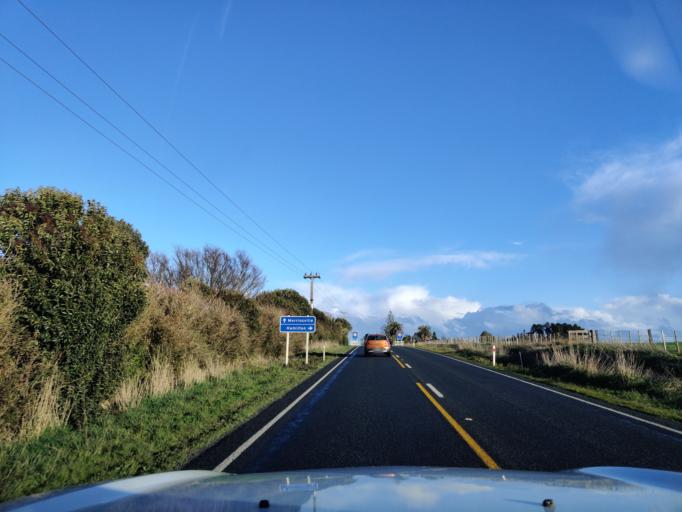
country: NZ
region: Waikato
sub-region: Hauraki District
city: Paeroa
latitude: -37.5865
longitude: 175.5019
